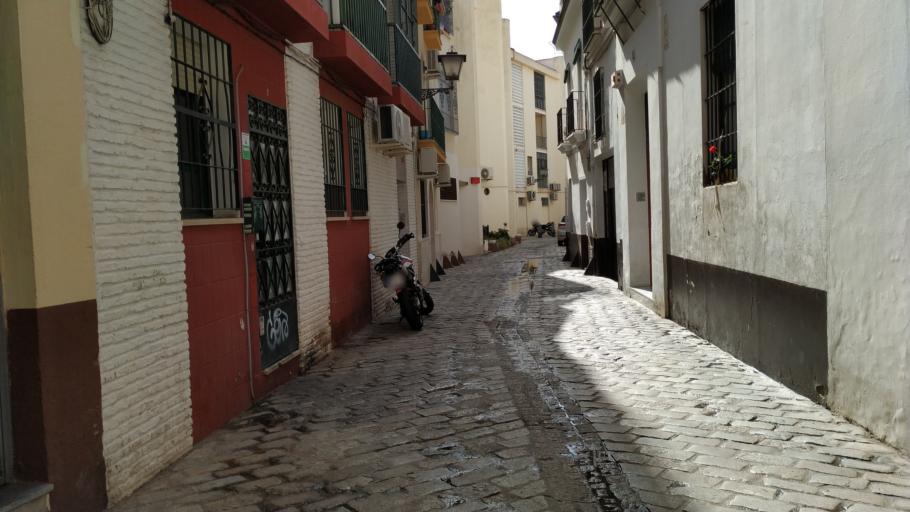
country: ES
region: Andalusia
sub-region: Provincia de Sevilla
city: Sevilla
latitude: 37.3882
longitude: -5.9879
